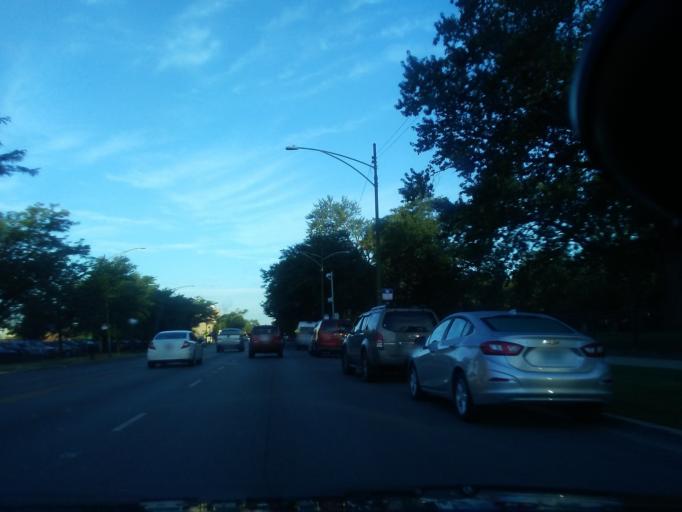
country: US
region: Illinois
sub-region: Cook County
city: Harwood Heights
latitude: 41.9533
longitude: -87.7628
